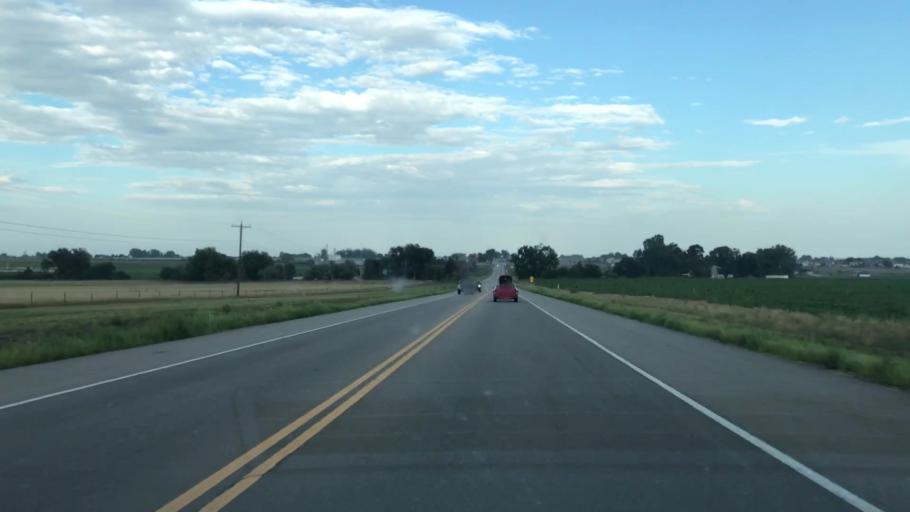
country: US
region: Colorado
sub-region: Weld County
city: Mead
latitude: 40.2038
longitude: -105.0232
